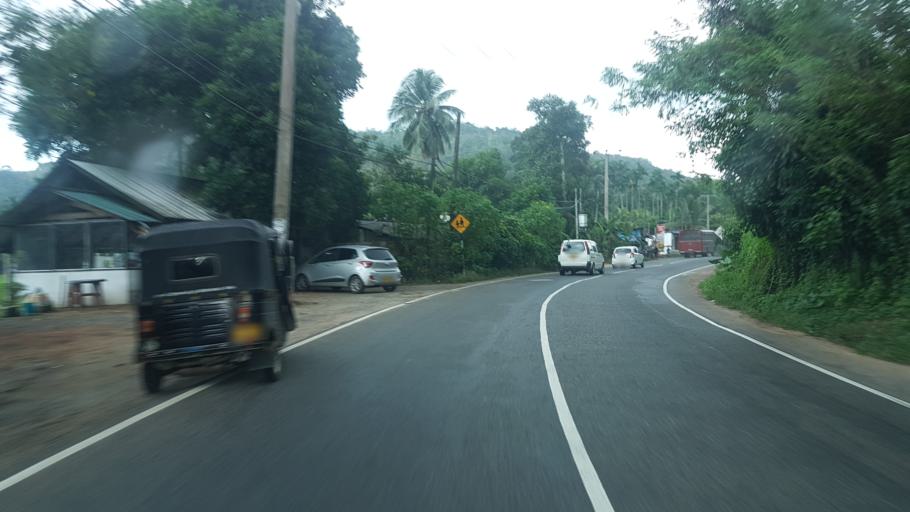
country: LK
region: Western
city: Hanwella Ihala
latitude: 6.9659
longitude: 80.2332
